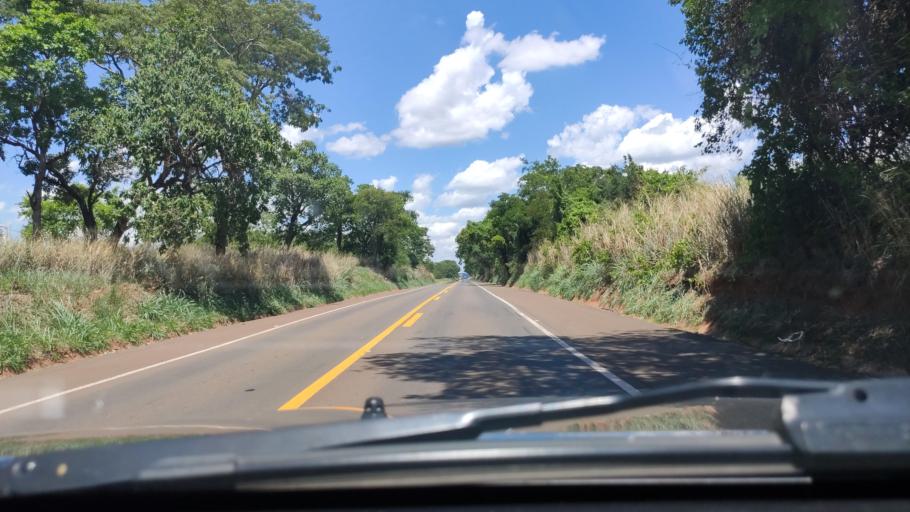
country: BR
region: Sao Paulo
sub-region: Boa Esperanca Do Sul
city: Boa Esperanca do Sul
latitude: -22.0694
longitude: -48.3961
